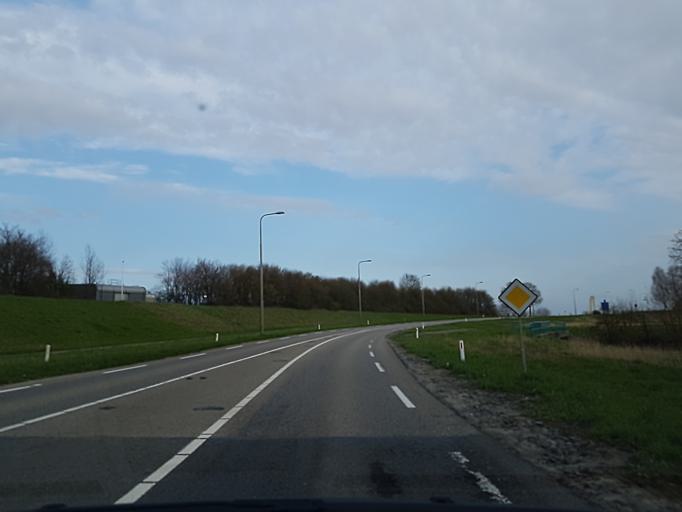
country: NL
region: Zeeland
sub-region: Gemeente Terneuzen
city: Terneuzen
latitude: 51.3314
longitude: 3.8108
